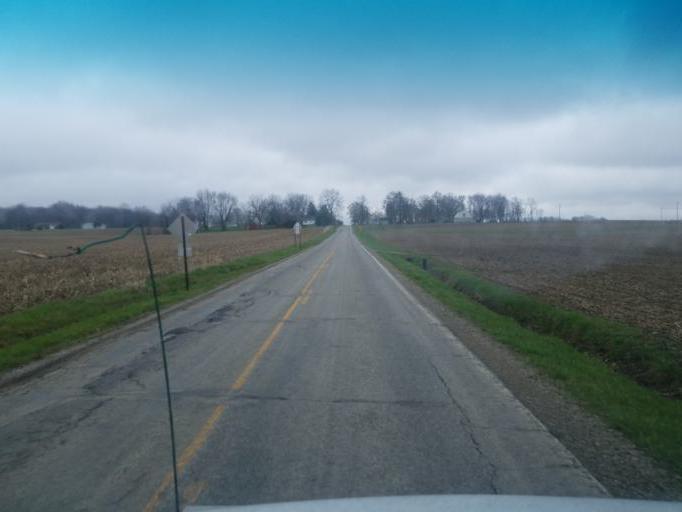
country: US
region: Ohio
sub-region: Richland County
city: Shelby
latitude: 40.9132
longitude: -82.6307
